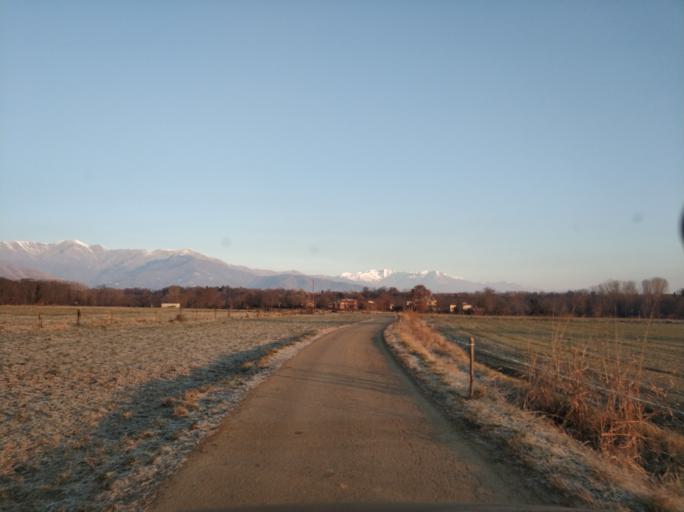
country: IT
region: Piedmont
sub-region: Provincia di Torino
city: Nole
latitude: 45.2481
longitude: 7.5694
